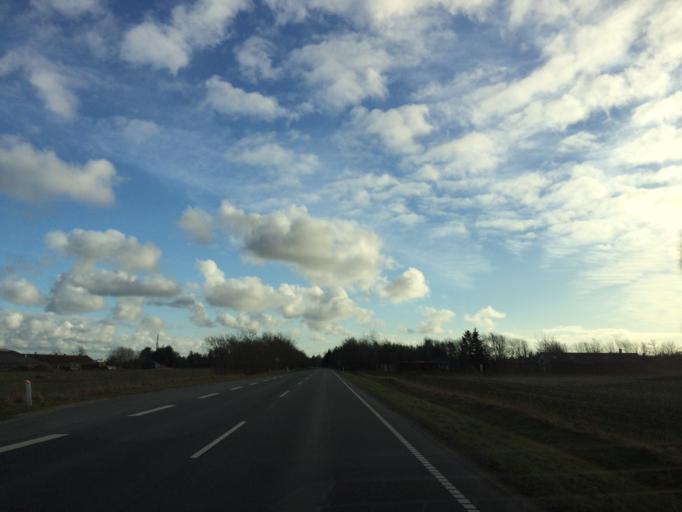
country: DK
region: Central Jutland
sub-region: Holstebro Kommune
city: Ulfborg
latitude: 56.3578
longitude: 8.3373
